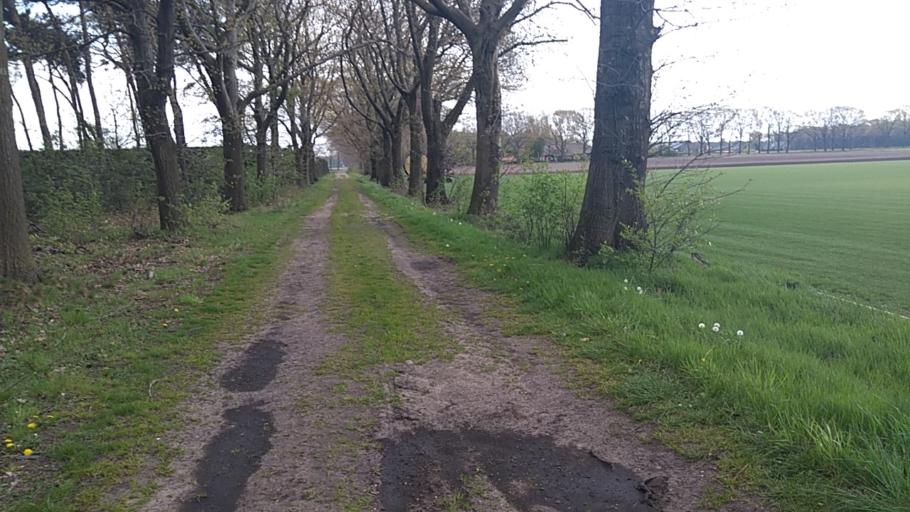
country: NL
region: Limburg
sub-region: Gemeente Leudal
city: Heythuysen
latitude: 51.3033
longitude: 5.8648
